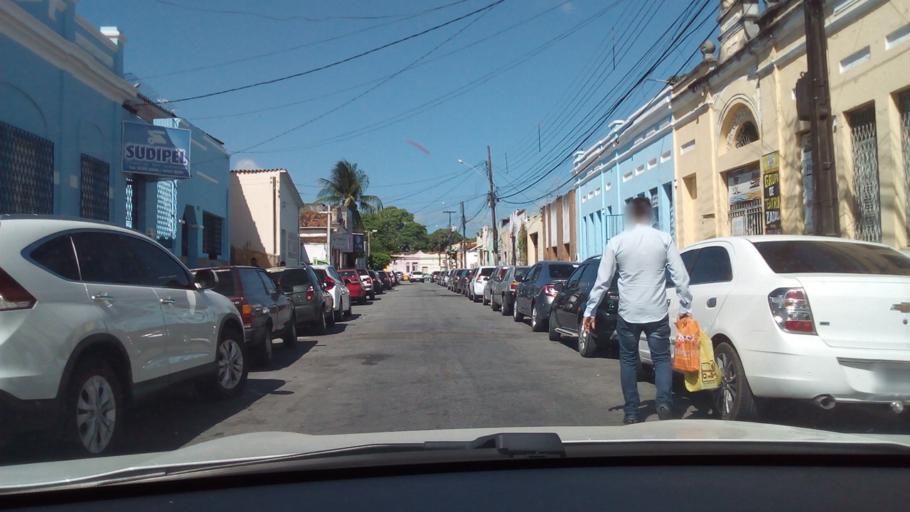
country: BR
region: Paraiba
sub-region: Joao Pessoa
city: Joao Pessoa
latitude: -7.1154
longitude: -34.8816
